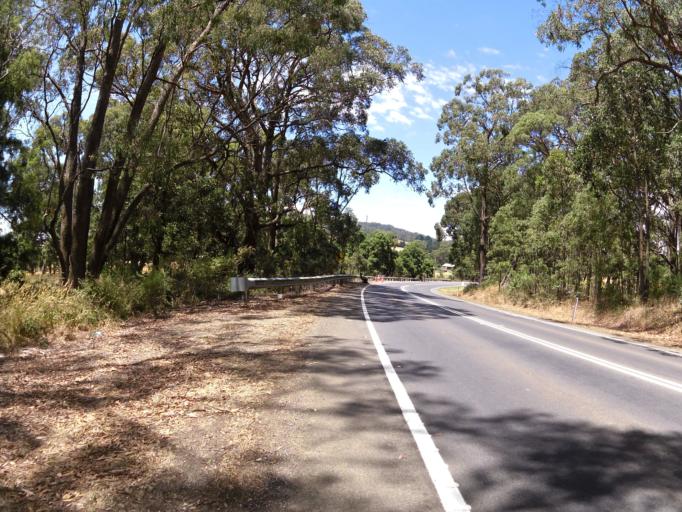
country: AU
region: Victoria
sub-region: Ballarat North
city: Mount Clear
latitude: -37.6376
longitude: 143.9147
